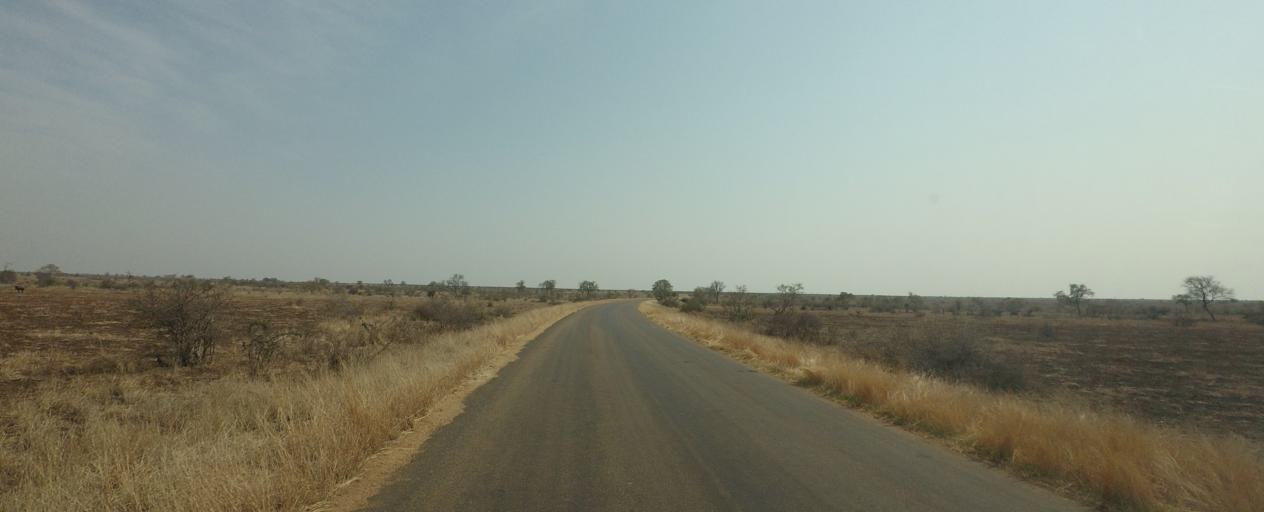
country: ZA
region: Limpopo
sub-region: Mopani District Municipality
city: Phalaborwa
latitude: -24.2686
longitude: 31.7300
